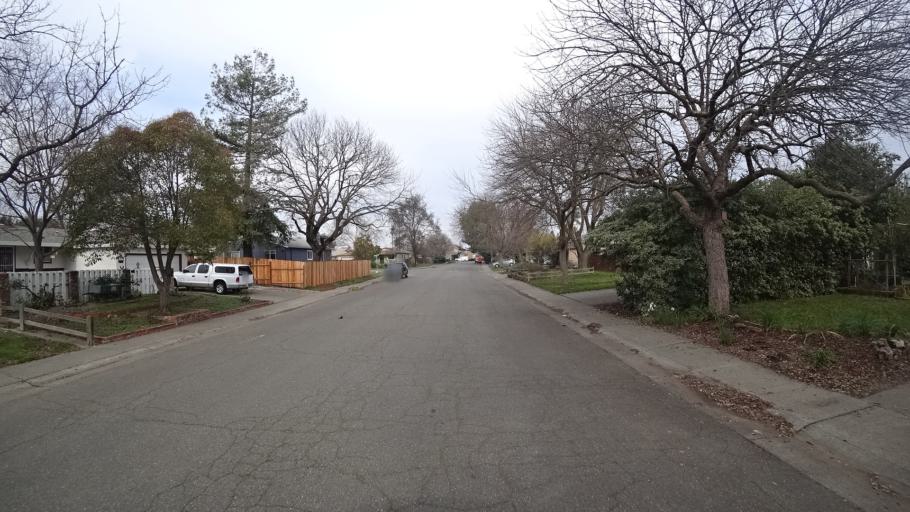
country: US
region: California
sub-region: Yolo County
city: Davis
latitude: 38.5591
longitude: -121.7326
